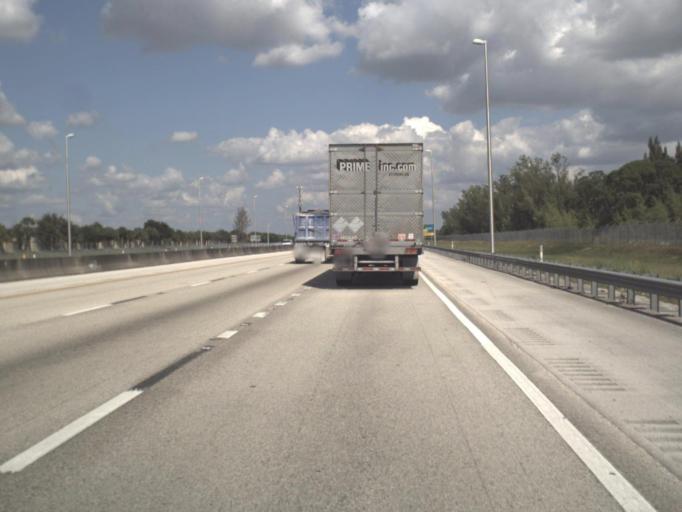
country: US
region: Florida
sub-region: Palm Beach County
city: Seminole Manor
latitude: 26.5498
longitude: -80.1727
